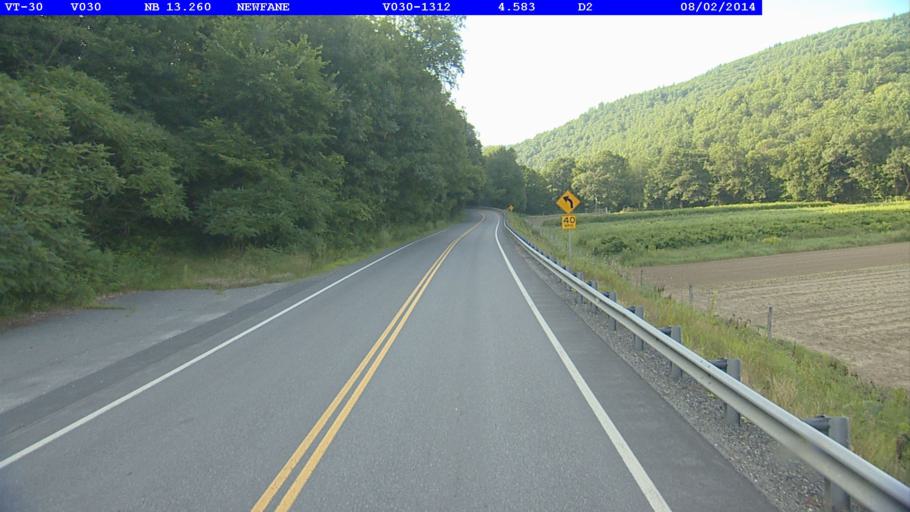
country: US
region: Vermont
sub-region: Windham County
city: Newfane
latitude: 43.0068
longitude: -72.6449
